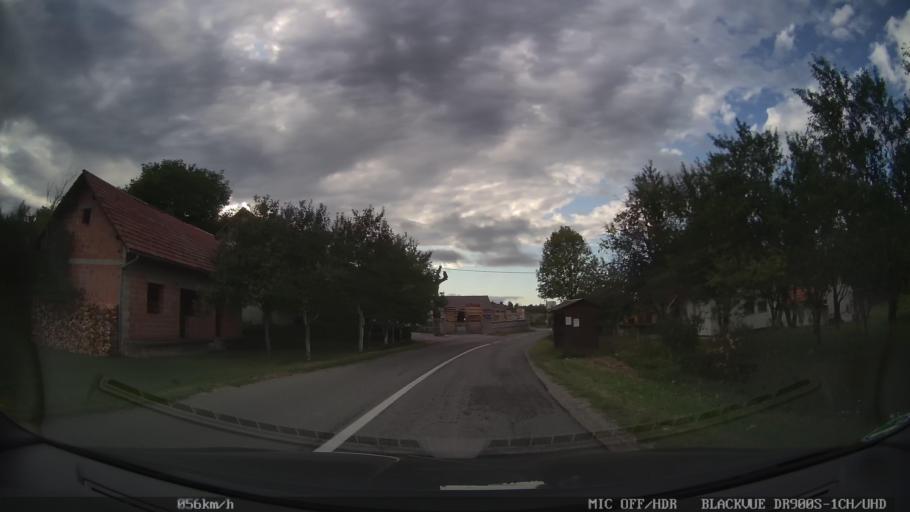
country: HR
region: Karlovacka
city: Plaski
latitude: 44.9847
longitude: 15.4726
